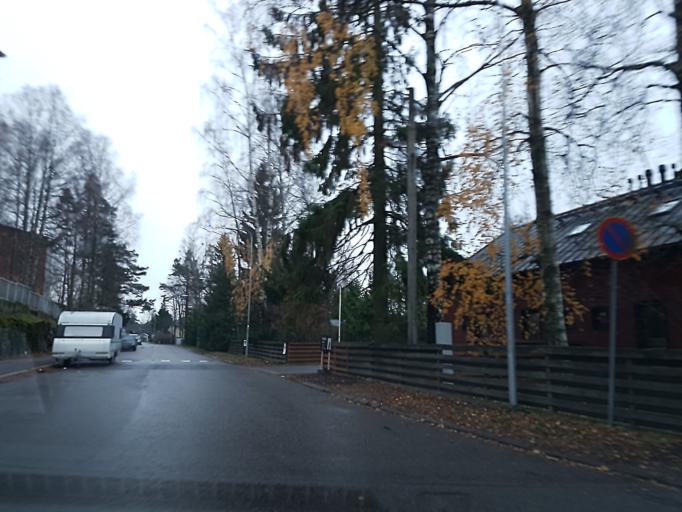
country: FI
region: Uusimaa
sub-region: Helsinki
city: Vantaa
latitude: 60.2426
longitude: 25.1003
